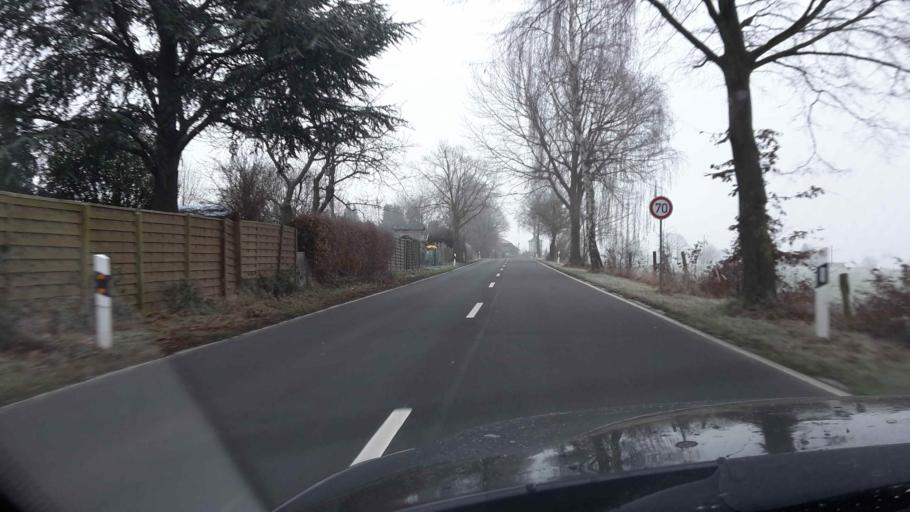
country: DE
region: North Rhine-Westphalia
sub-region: Regierungsbezirk Koln
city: Hennef
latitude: 50.7312
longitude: 7.2909
